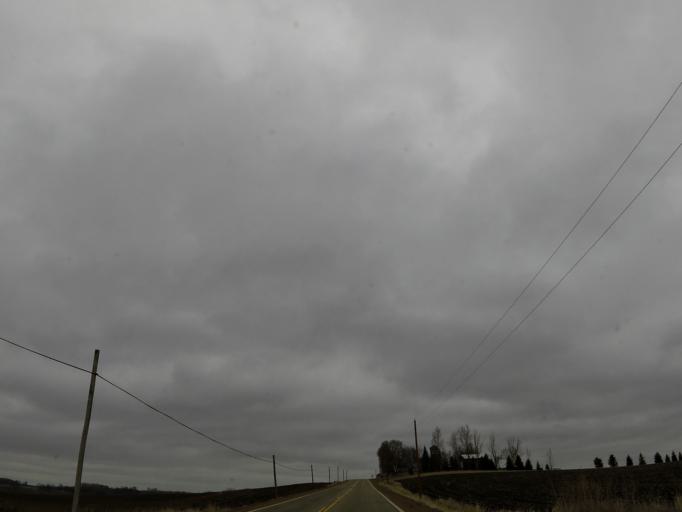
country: US
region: Minnesota
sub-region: Scott County
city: Shakopee
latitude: 44.7106
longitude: -93.5413
